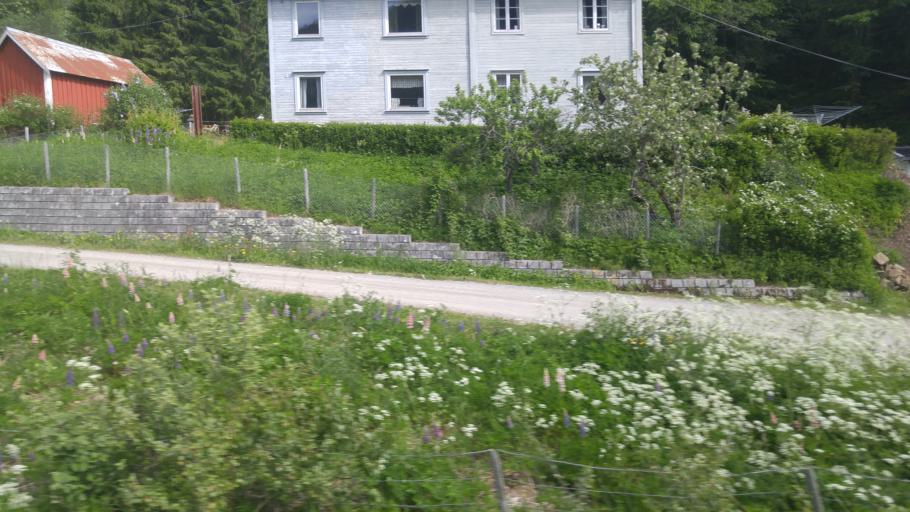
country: NO
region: Sor-Trondelag
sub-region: Midtre Gauldal
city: Storen
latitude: 63.0200
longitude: 10.4290
